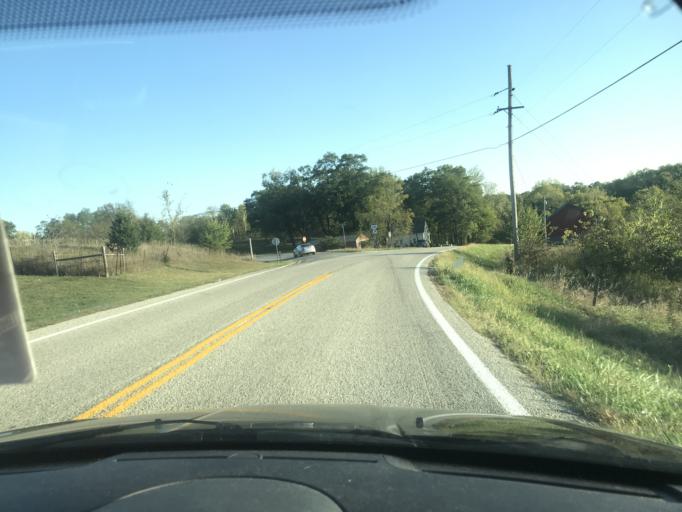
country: US
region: Ohio
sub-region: Logan County
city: De Graff
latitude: 40.2521
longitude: -83.8691
